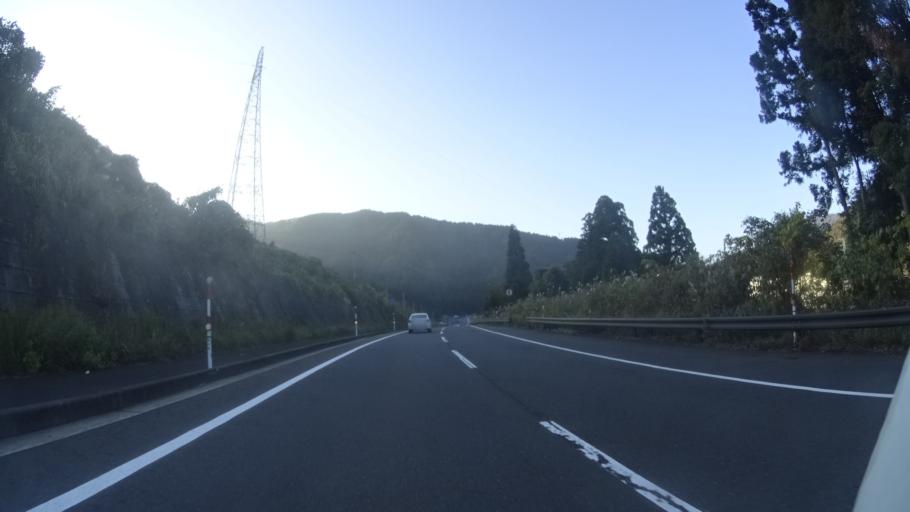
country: JP
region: Fukui
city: Ono
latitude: 35.9960
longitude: 136.3631
